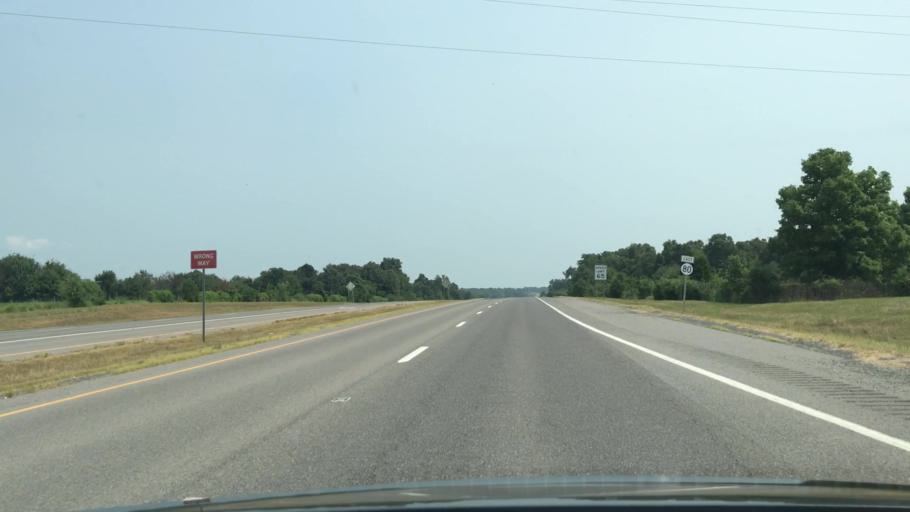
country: US
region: Kentucky
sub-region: Calloway County
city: Murray
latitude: 36.7413
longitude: -88.1644
